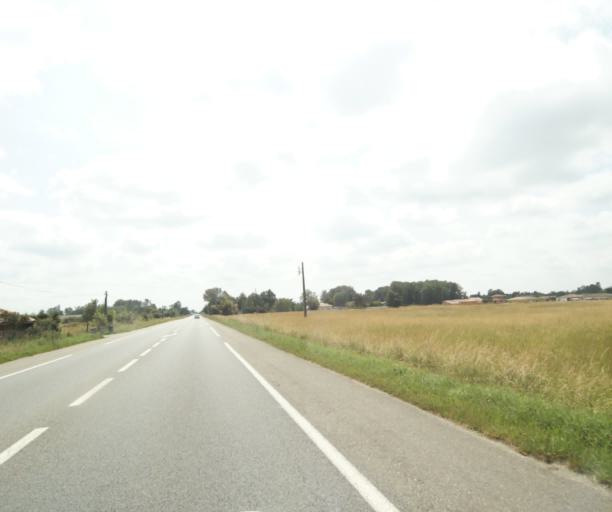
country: FR
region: Midi-Pyrenees
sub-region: Departement du Tarn-et-Garonne
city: Albias
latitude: 44.0651
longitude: 1.4151
